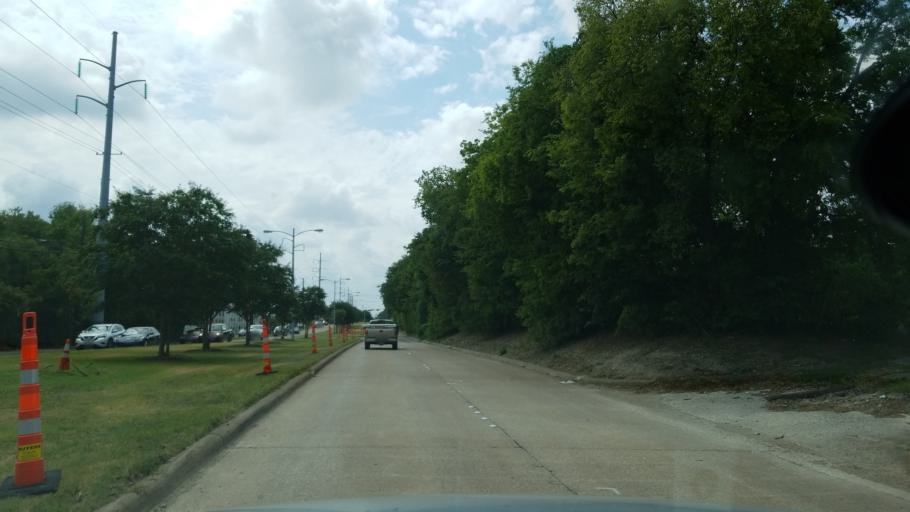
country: US
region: Texas
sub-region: Dallas County
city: Garland
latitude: 32.9262
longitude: -96.6653
